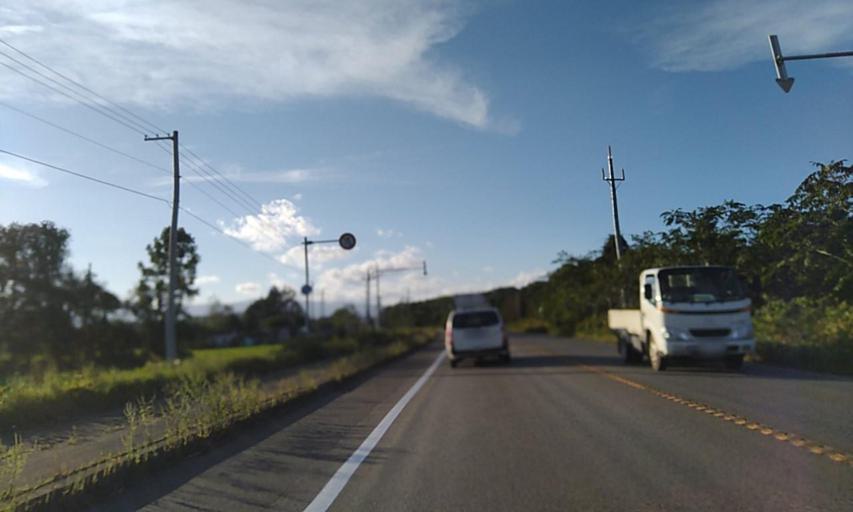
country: JP
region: Hokkaido
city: Obihiro
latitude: 42.9317
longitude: 142.9772
